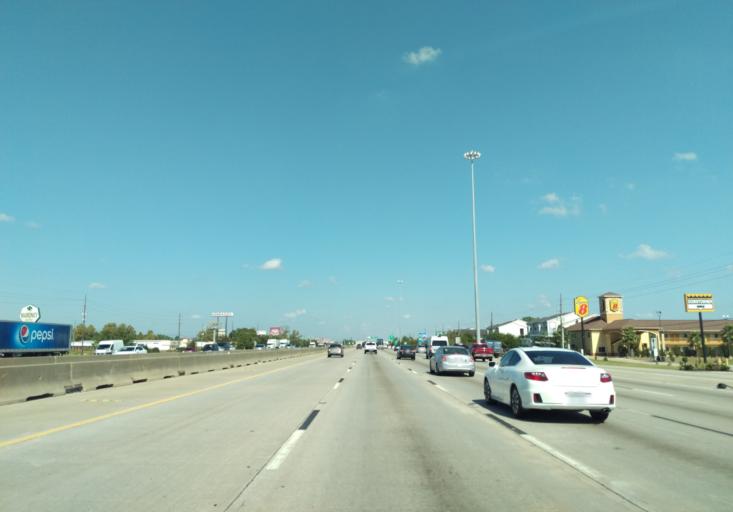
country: US
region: Texas
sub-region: Harris County
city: Spring
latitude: 30.0022
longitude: -95.4263
